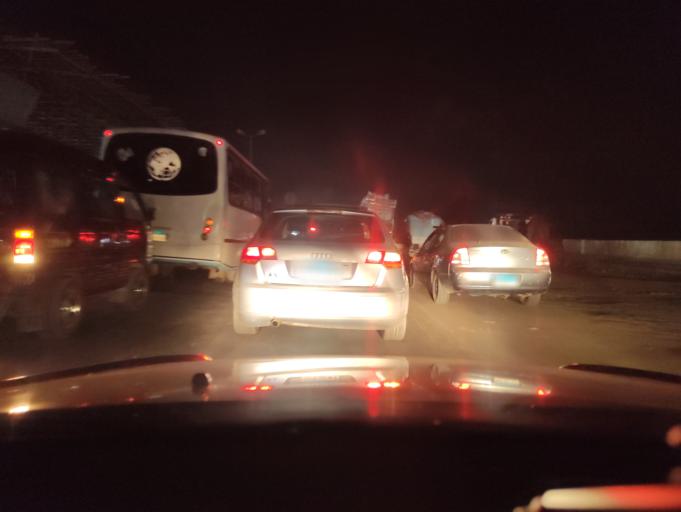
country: EG
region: Muhafazat al Qalyubiyah
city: Banha
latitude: 30.5050
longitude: 31.1622
